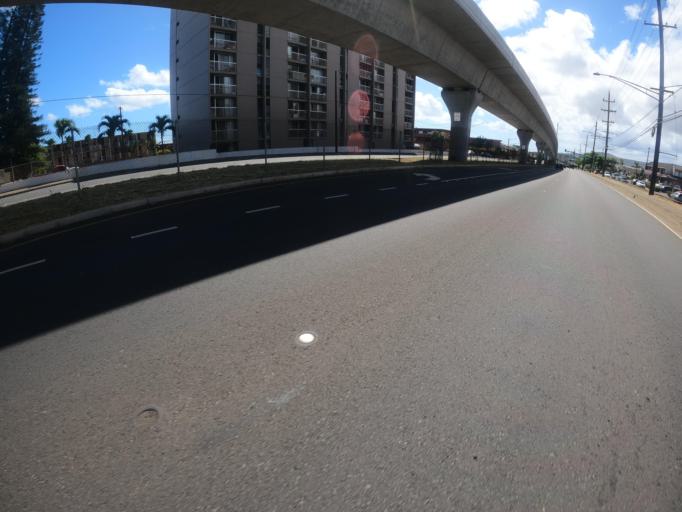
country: US
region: Hawaii
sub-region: Honolulu County
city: Waipahu
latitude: 21.3814
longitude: -158.0165
